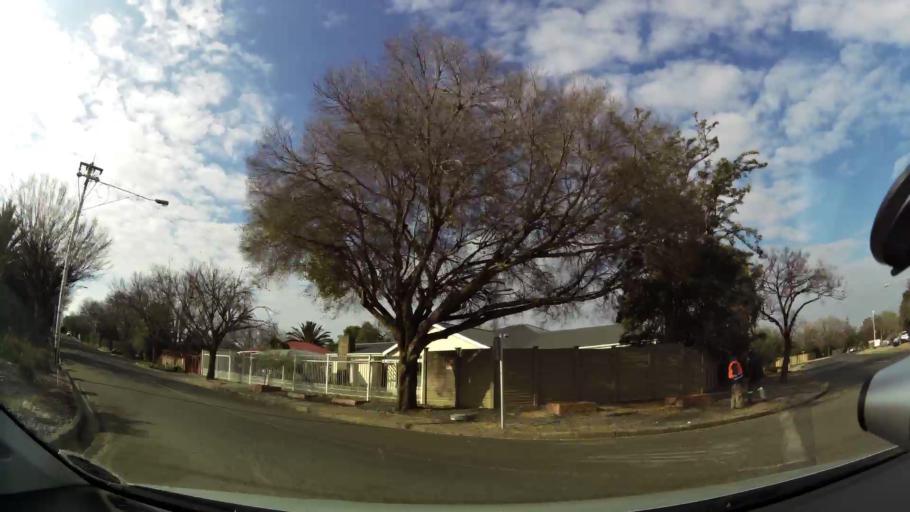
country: ZA
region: Orange Free State
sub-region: Mangaung Metropolitan Municipality
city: Bloemfontein
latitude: -29.0808
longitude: 26.2137
